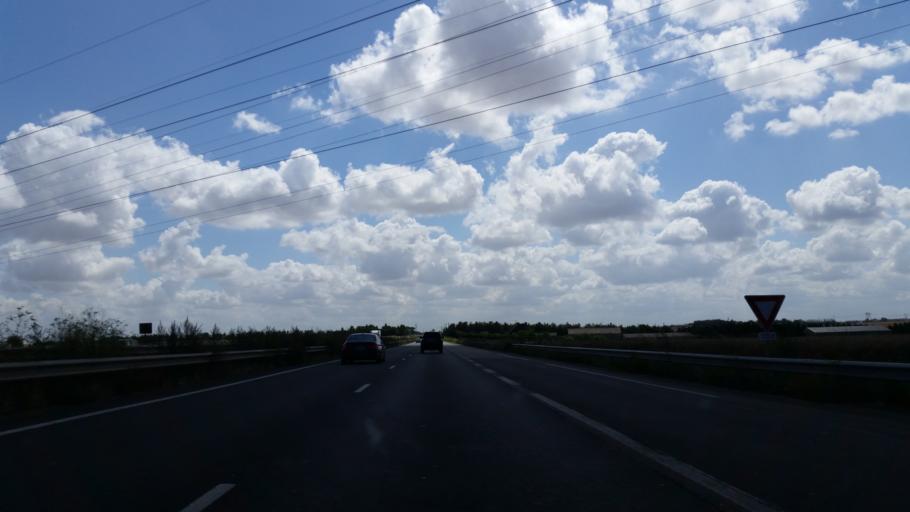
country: FR
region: Lower Normandy
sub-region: Departement du Calvados
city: Ifs
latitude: 49.1342
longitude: -0.3325
